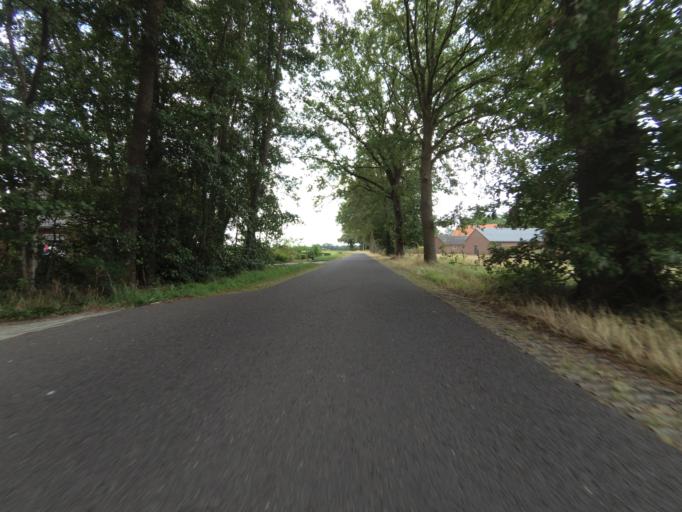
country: NL
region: Overijssel
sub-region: Gemeente Hof van Twente
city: Hengevelde
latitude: 52.1678
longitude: 6.6818
